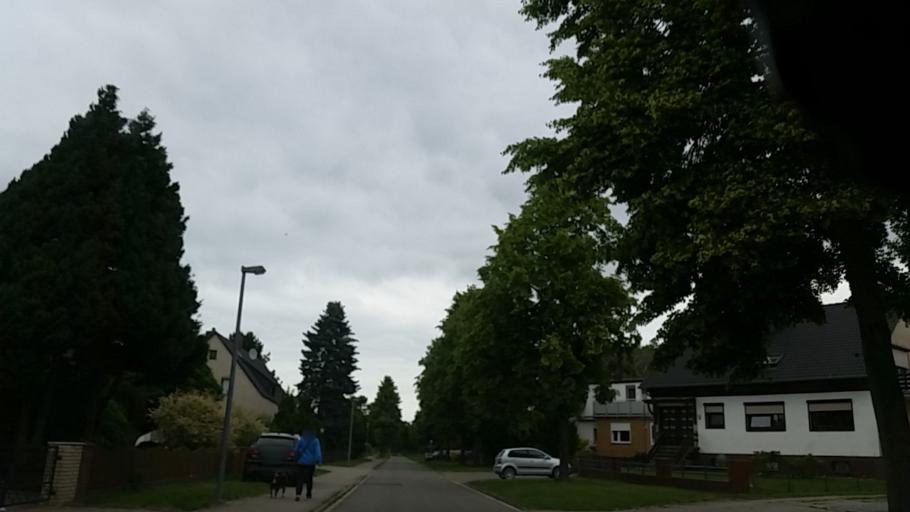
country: DE
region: Lower Saxony
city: Danndorf
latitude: 52.3929
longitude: 10.8574
